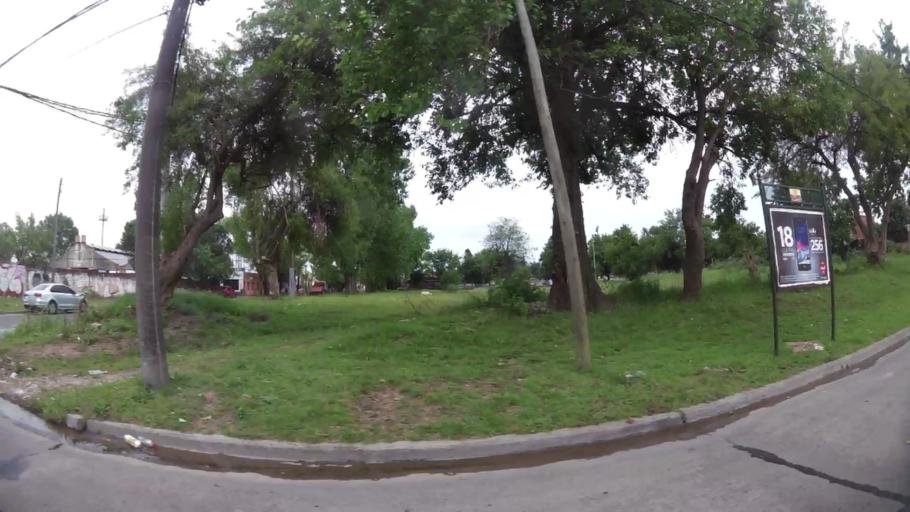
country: AR
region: Buenos Aires
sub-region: Partido de Campana
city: Campana
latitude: -34.1764
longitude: -58.9479
